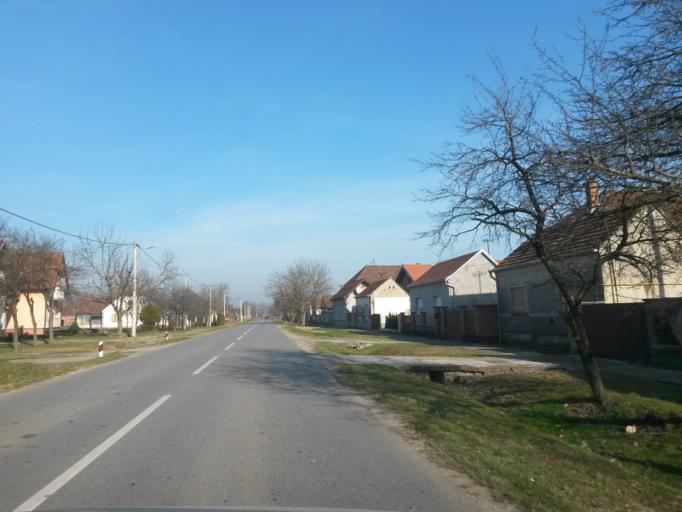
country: HR
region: Vukovarsko-Srijemska
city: Privlaka
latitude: 45.2048
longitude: 18.8505
